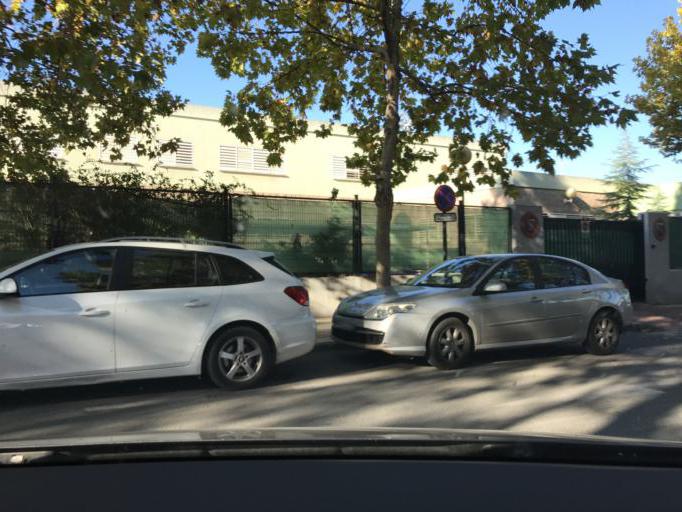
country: ES
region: Andalusia
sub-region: Provincia de Granada
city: Maracena
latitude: 37.2099
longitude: -3.6274
